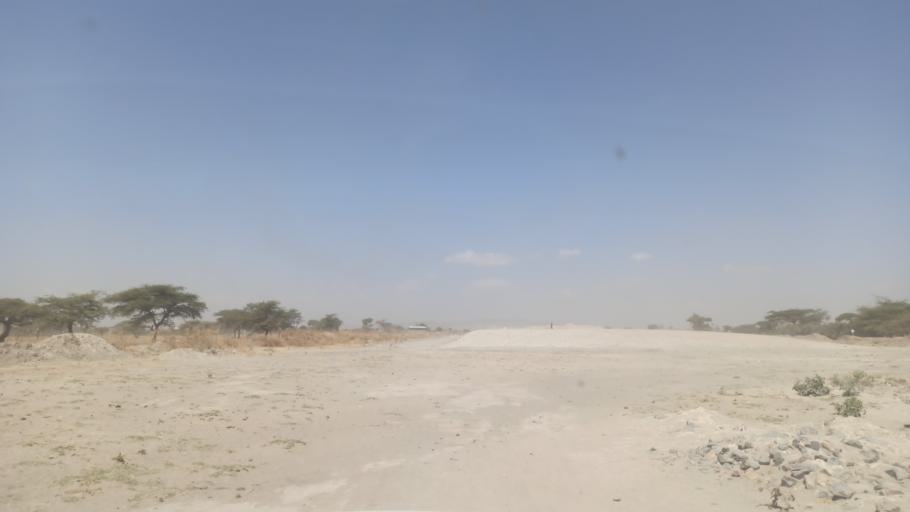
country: ET
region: Oromiya
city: Ziway
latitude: 7.7192
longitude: 38.6315
